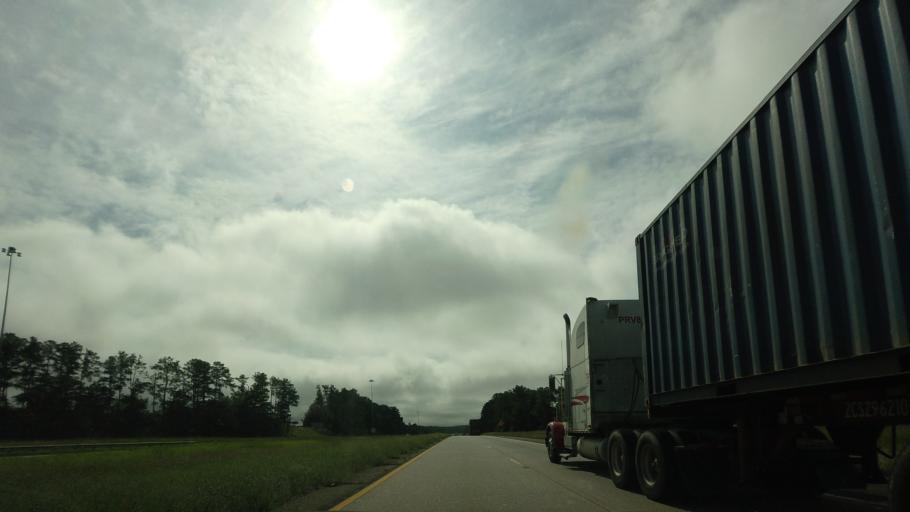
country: US
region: Georgia
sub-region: Bibb County
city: Macon
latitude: 32.7979
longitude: -83.5682
